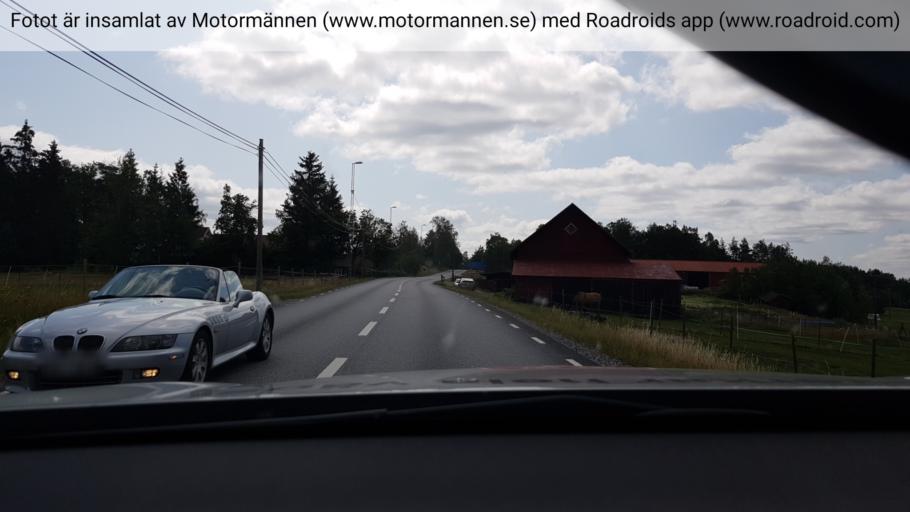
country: SE
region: Stockholm
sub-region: Vallentuna Kommun
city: Vallentuna
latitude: 59.5401
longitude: 18.1700
